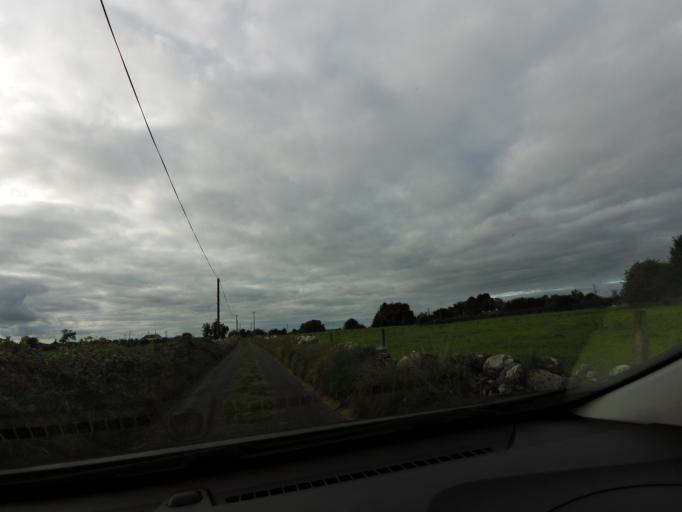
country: IE
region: Connaught
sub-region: County Galway
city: Ballinasloe
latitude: 53.3589
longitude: -8.0952
